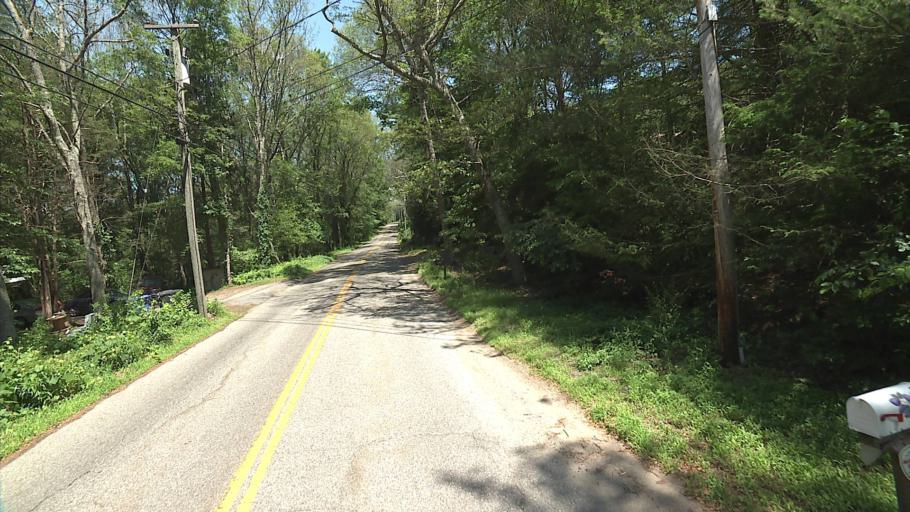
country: US
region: Connecticut
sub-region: New London County
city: Preston City
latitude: 41.5256
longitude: -71.8796
